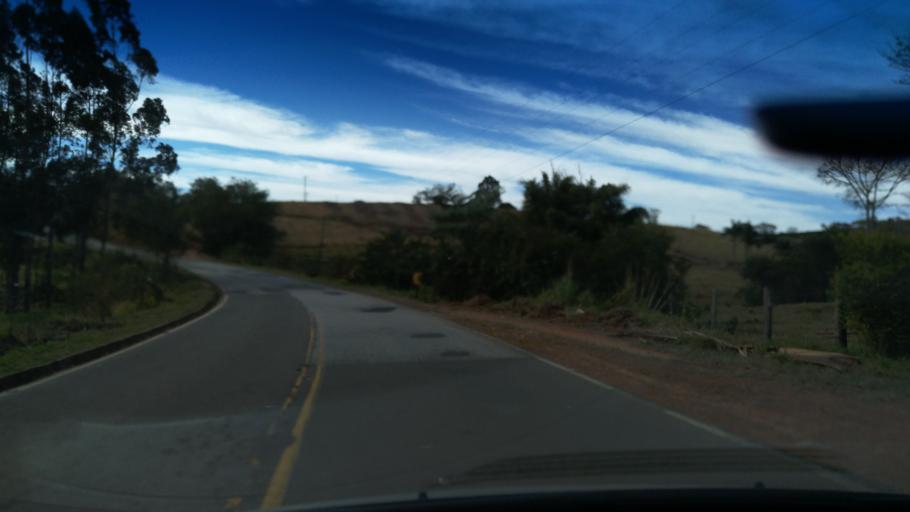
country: BR
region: Minas Gerais
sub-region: Andradas
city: Andradas
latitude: -22.0573
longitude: -46.4272
